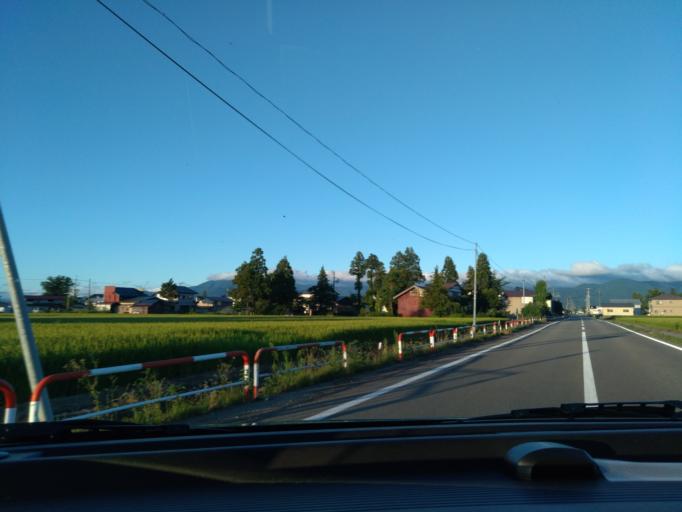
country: JP
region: Akita
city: Omagari
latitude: 39.4861
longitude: 140.5325
